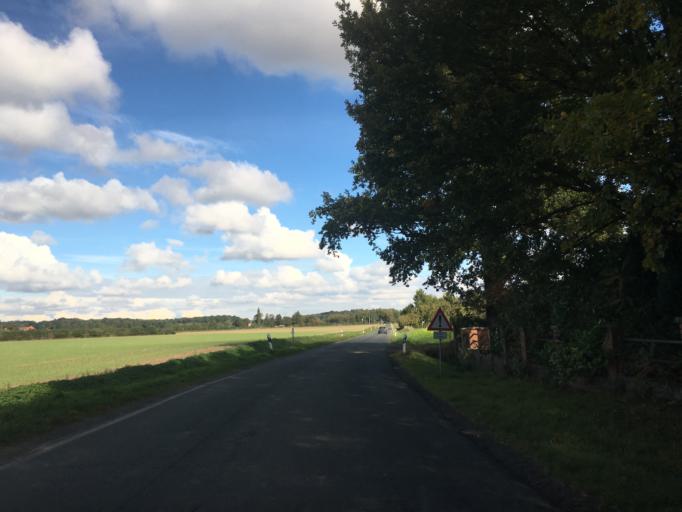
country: DE
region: North Rhine-Westphalia
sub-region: Regierungsbezirk Munster
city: Havixbeck
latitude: 51.9796
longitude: 7.4706
